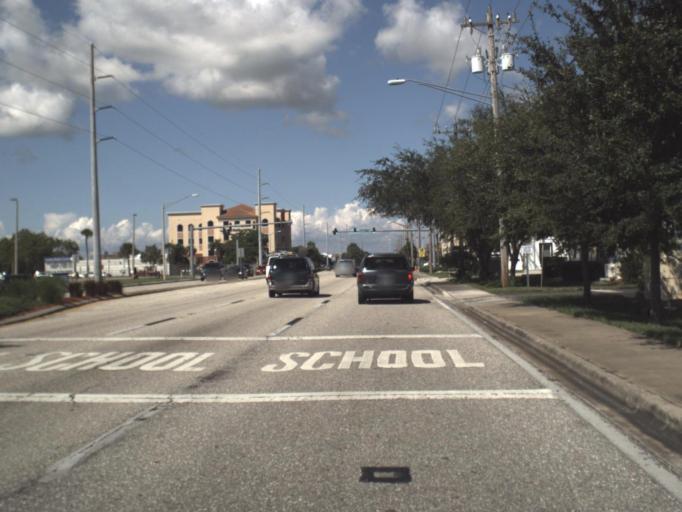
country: US
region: Florida
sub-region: Lee County
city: Lochmoor Waterway Estates
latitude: 26.6428
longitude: -81.9408
